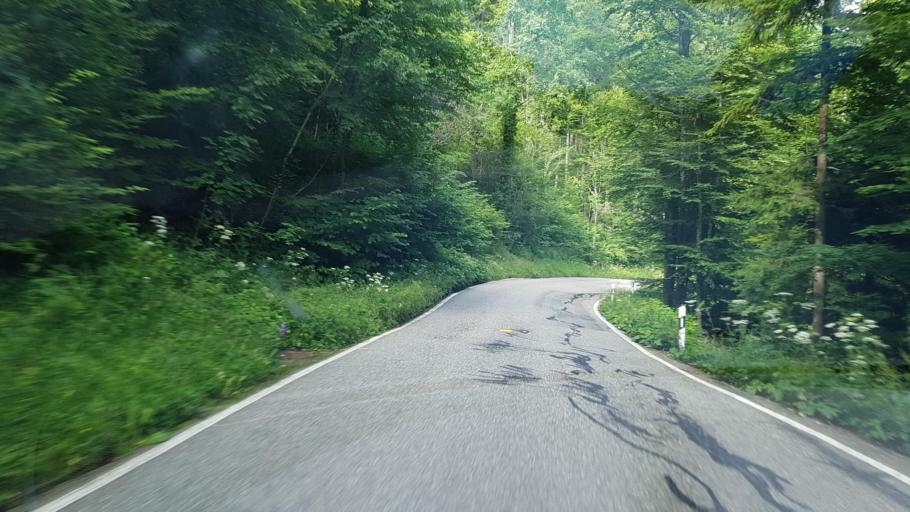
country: CH
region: Solothurn
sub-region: Bezirk Lebern
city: Riedholz
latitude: 47.2612
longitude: 7.5600
